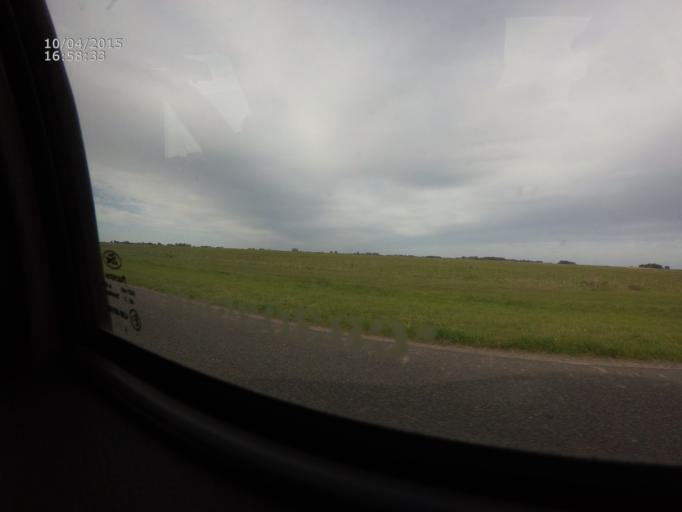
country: AR
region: Buenos Aires
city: Coronel Vidal
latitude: -37.4902
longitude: -57.7173
